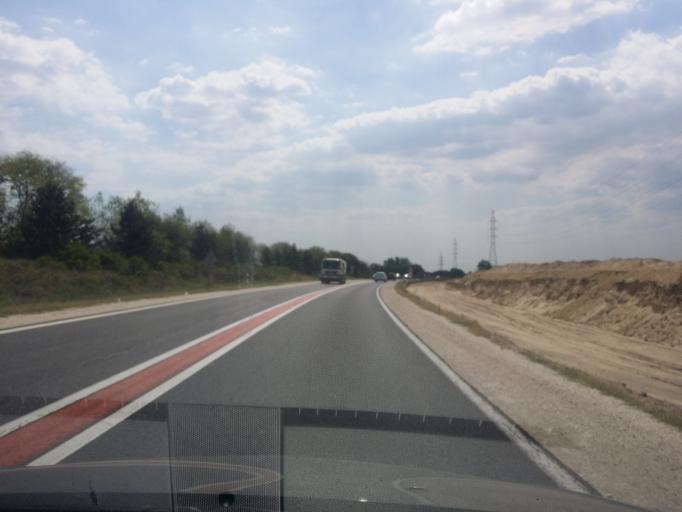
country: HU
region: Pest
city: Fot
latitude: 47.6340
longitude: 19.1696
